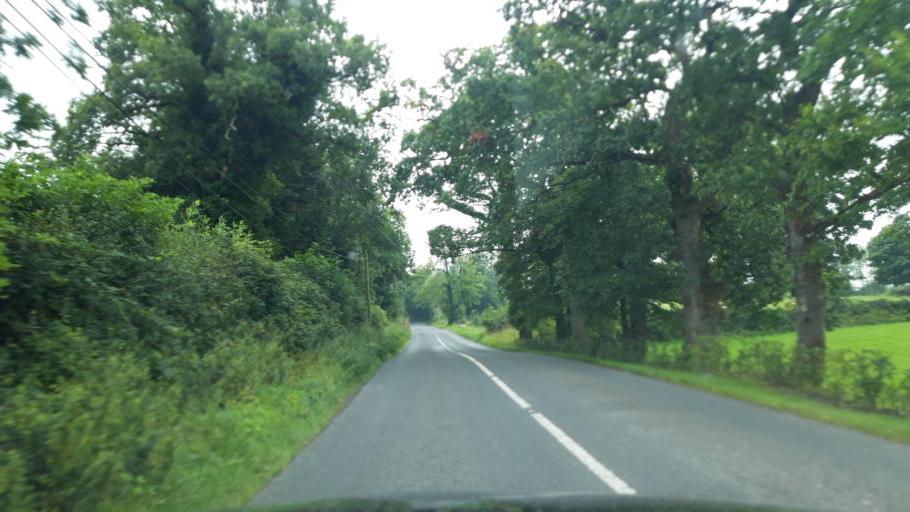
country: IE
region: Munster
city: Fethard
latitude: 52.5425
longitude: -7.6817
